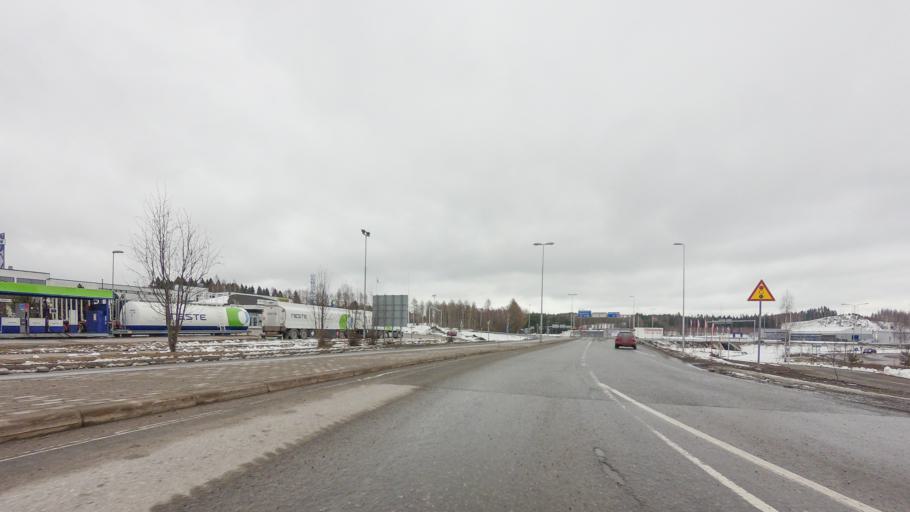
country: FI
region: Southern Savonia
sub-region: Savonlinna
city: Savonlinna
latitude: 61.8764
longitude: 28.9510
